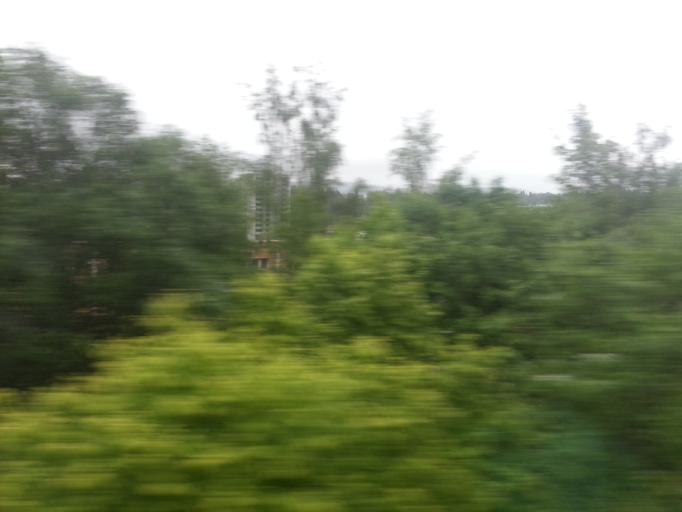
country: NO
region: Sor-Trondelag
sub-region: Trondheim
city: Trondheim
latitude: 63.3771
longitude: 10.3561
